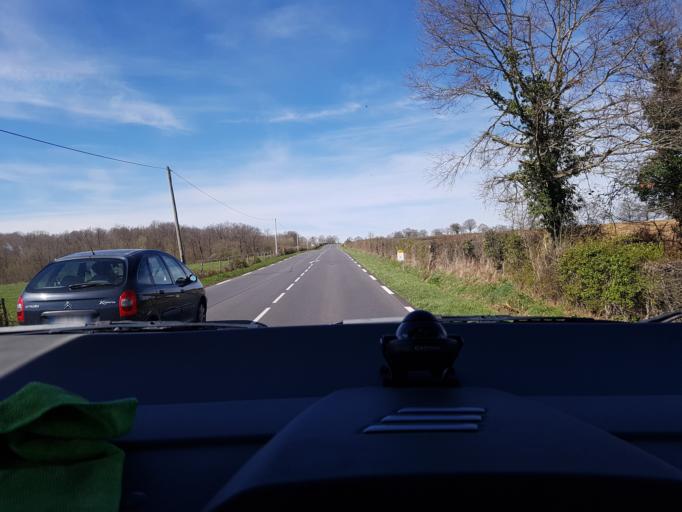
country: FR
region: Auvergne
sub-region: Departement de l'Allier
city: Le Donjon
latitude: 46.3435
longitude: 3.7855
